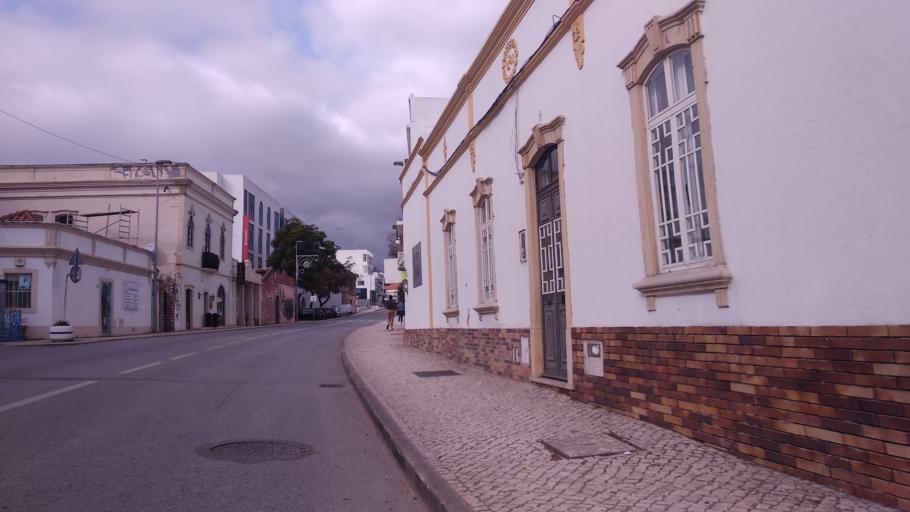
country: PT
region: Faro
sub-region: Loule
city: Almancil
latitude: 37.0874
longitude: -8.0326
